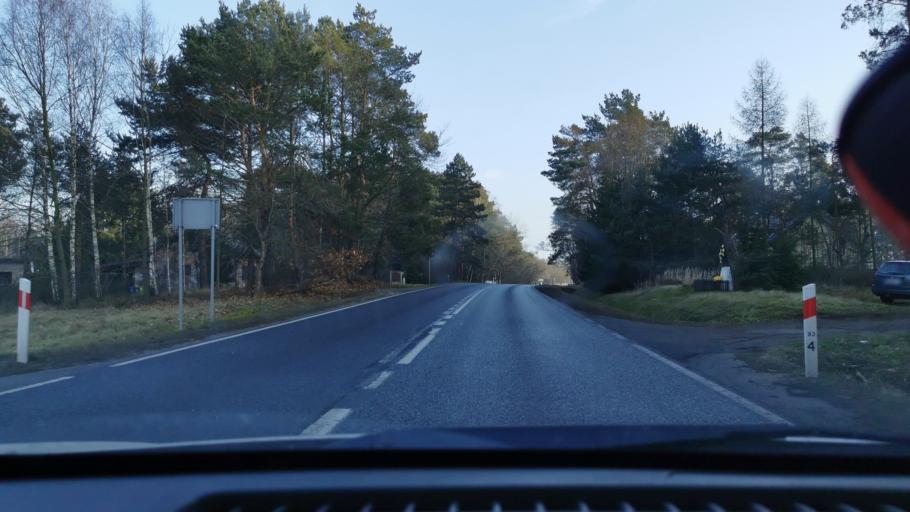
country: PL
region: Lodz Voivodeship
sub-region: Powiat laski
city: Lask
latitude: 51.5721
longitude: 19.1839
